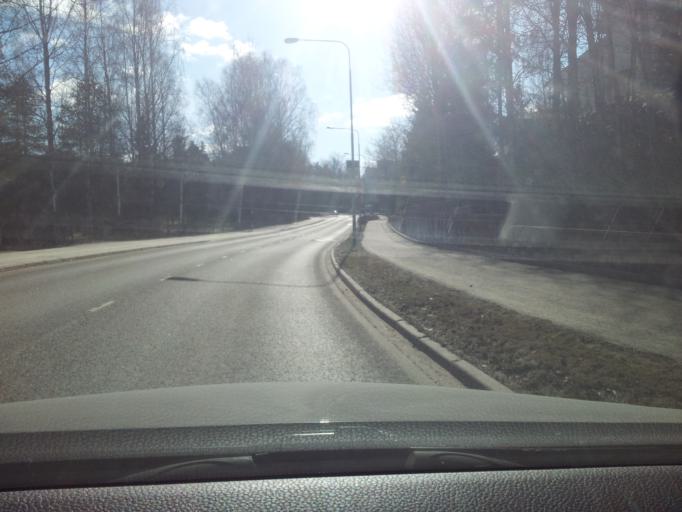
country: FI
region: Uusimaa
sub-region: Helsinki
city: Koukkuniemi
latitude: 60.1619
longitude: 24.7910
